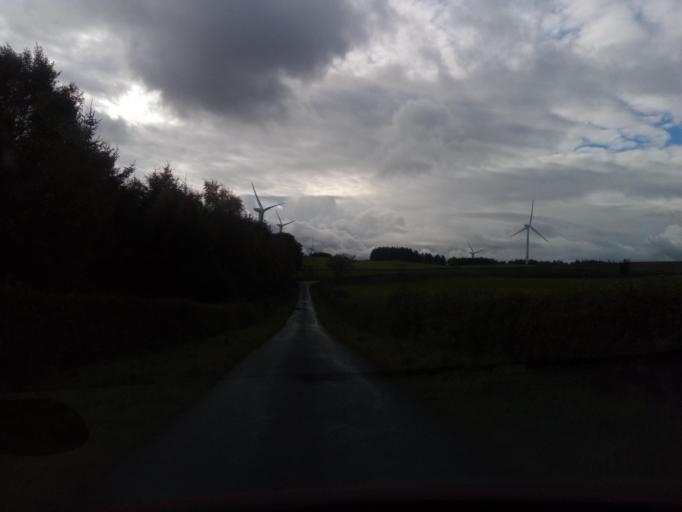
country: GB
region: Scotland
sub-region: The Scottish Borders
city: Galashiels
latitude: 55.6811
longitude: -2.8385
